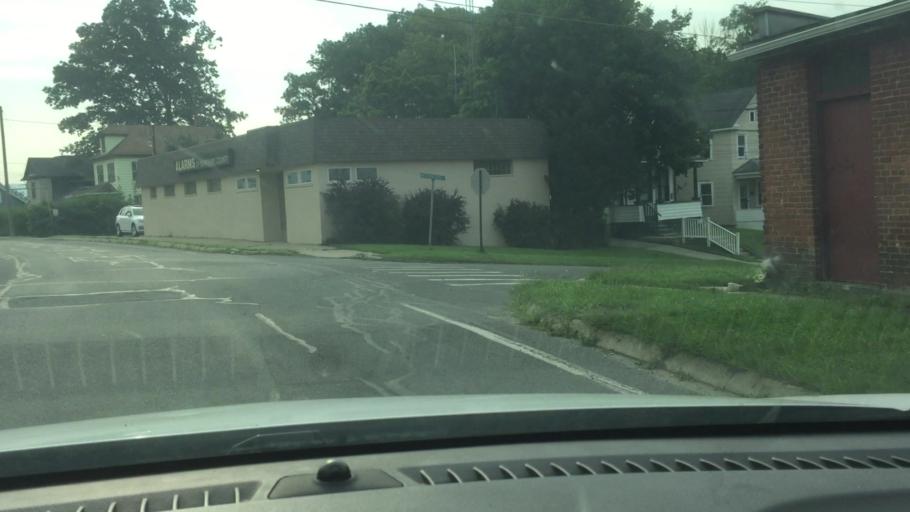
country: US
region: Massachusetts
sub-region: Berkshire County
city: Pittsfield
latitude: 42.4590
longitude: -73.2329
